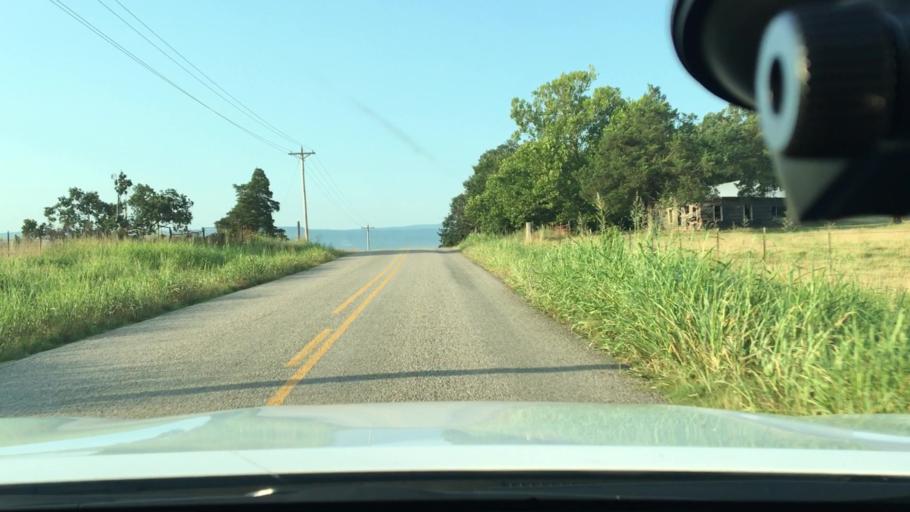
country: US
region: Arkansas
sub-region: Johnson County
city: Coal Hill
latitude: 35.3514
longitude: -93.6133
